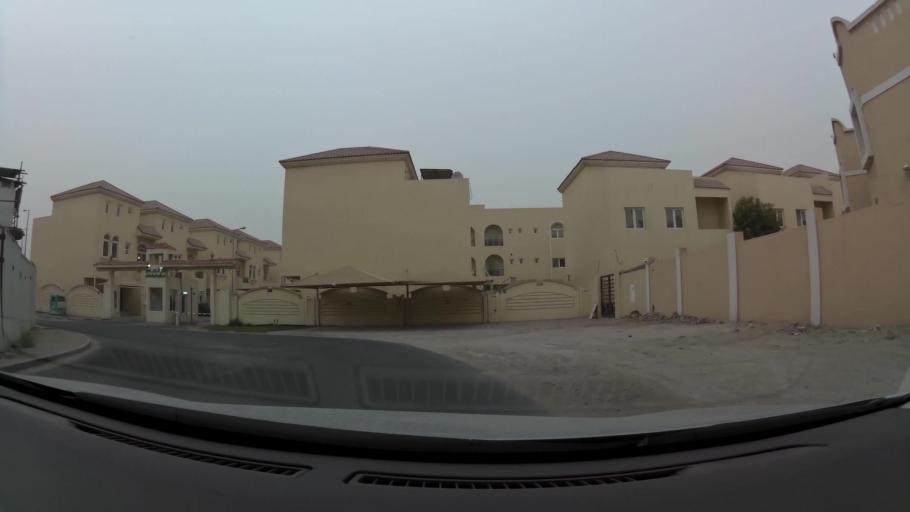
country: QA
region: Baladiyat ad Dawhah
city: Doha
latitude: 25.2447
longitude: 51.4878
